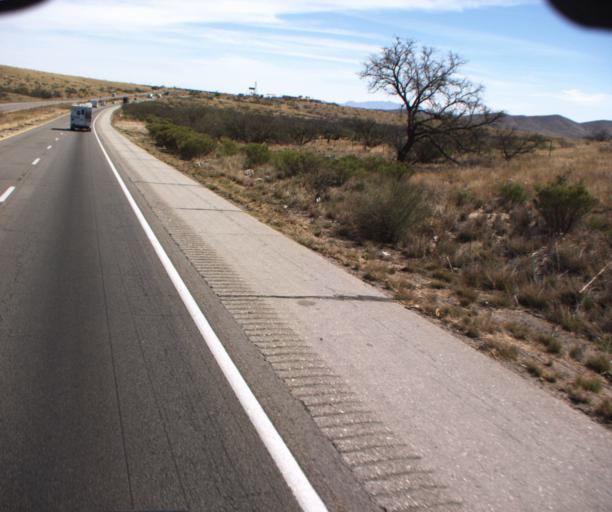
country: US
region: Arizona
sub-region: Cochise County
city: Saint David
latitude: 32.0752
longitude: -110.0617
